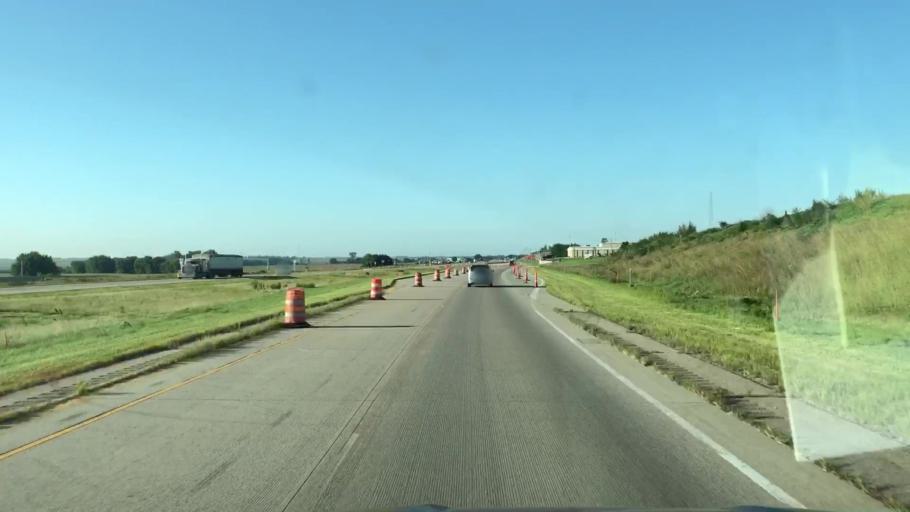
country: US
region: Iowa
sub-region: Plymouth County
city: Le Mars
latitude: 42.7524
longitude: -96.2104
